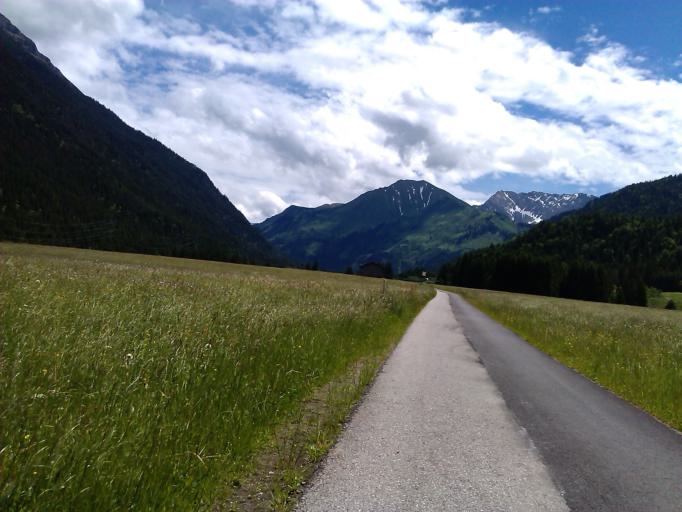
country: AT
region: Tyrol
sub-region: Politischer Bezirk Reutte
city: Heiterwang
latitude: 47.4420
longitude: 10.7536
